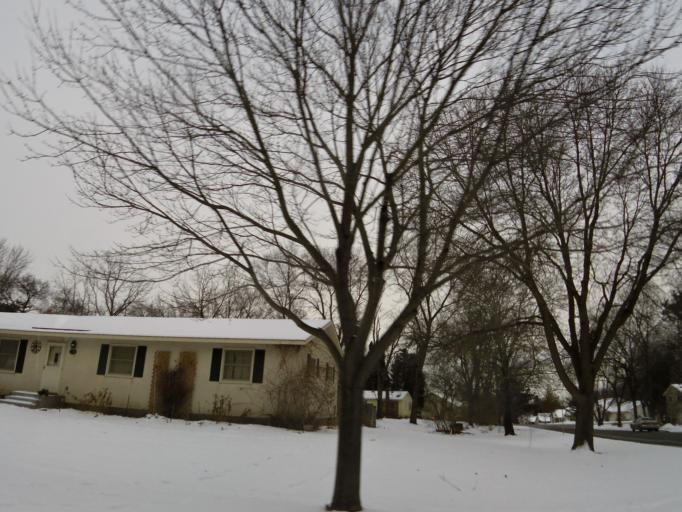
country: US
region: Minnesota
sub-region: Washington County
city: Oak Park Heights
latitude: 45.0313
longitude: -92.8087
